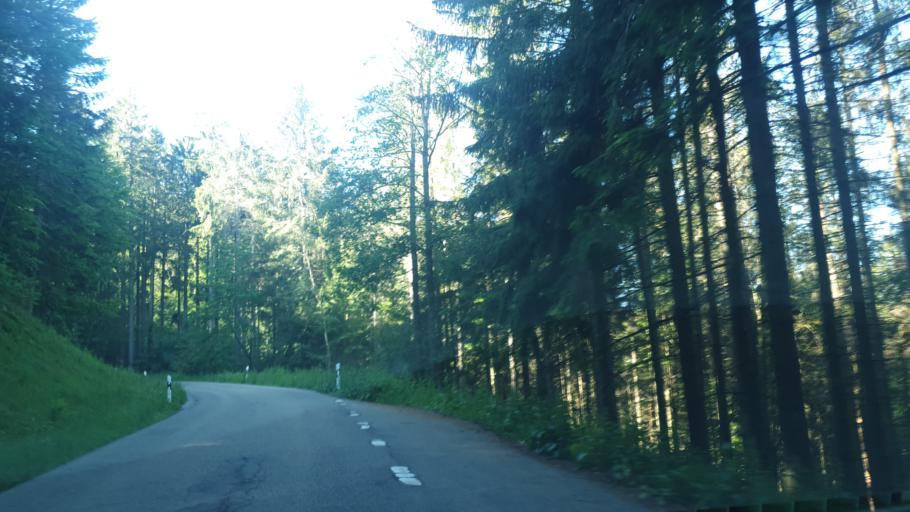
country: DE
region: Baden-Wuerttemberg
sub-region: Freiburg Region
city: Horben
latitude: 47.9045
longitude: 7.8695
